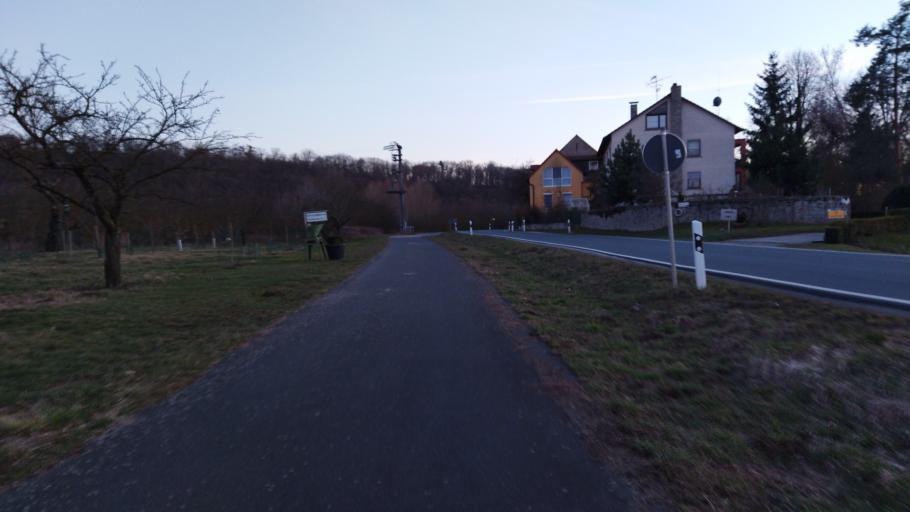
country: DE
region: Bavaria
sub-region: Regierungsbezirk Unterfranken
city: Nordheim
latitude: 49.8883
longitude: 10.1823
